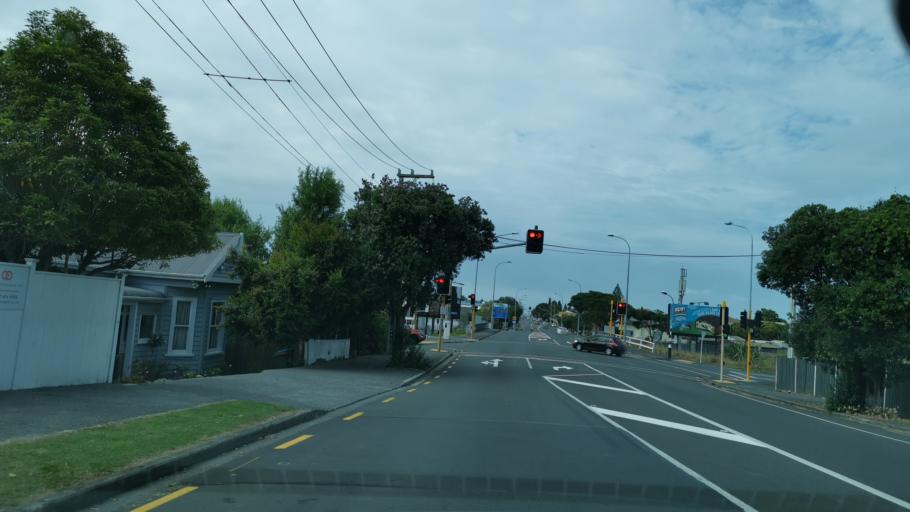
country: NZ
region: Auckland
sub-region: Auckland
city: Rosebank
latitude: -36.8937
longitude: 174.7009
